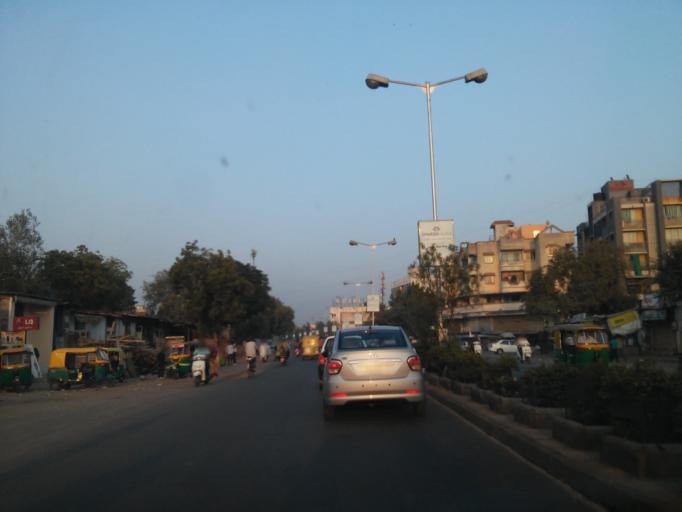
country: IN
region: Gujarat
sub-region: Ahmadabad
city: Sarkhej
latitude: 22.9987
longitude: 72.5434
